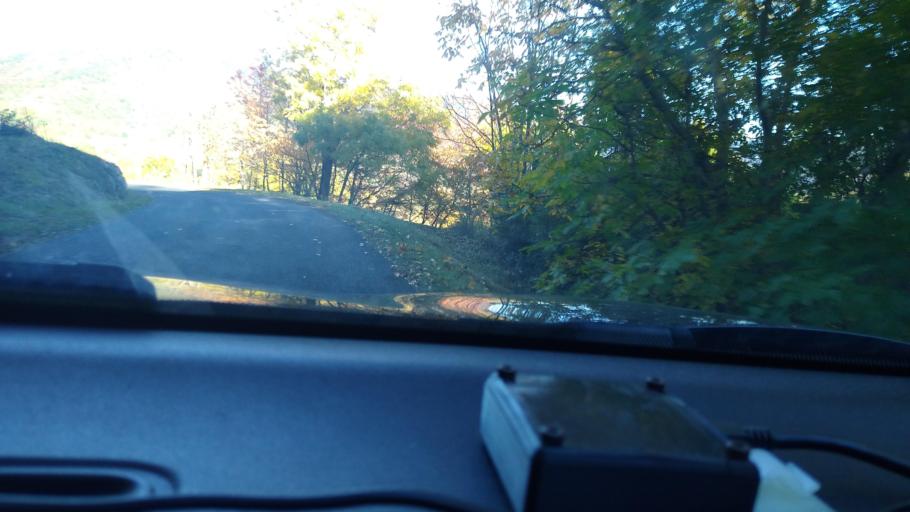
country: FR
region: Languedoc-Roussillon
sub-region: Departement de l'Aude
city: Quillan
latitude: 42.7391
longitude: 2.1595
